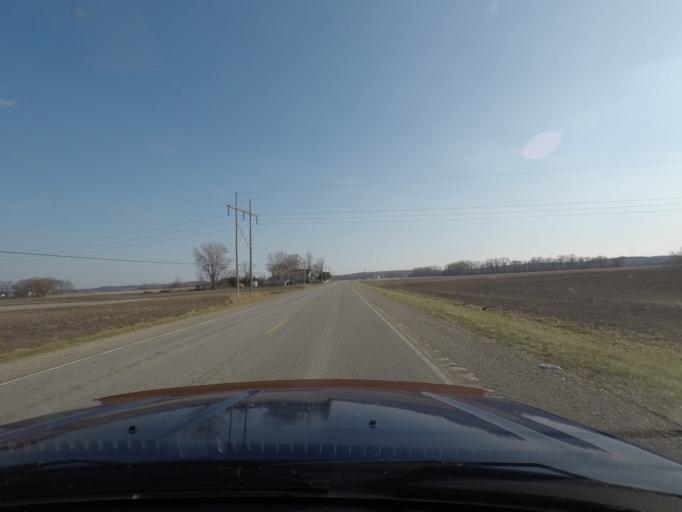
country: US
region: Kansas
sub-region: Jefferson County
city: Oskaloosa
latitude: 39.0652
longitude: -95.3820
